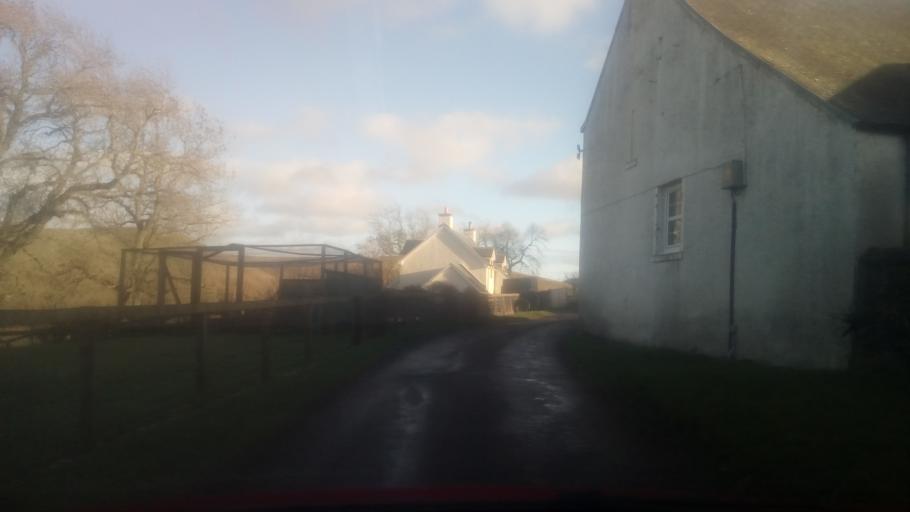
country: GB
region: Scotland
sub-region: The Scottish Borders
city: Kelso
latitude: 55.4493
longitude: -2.3707
